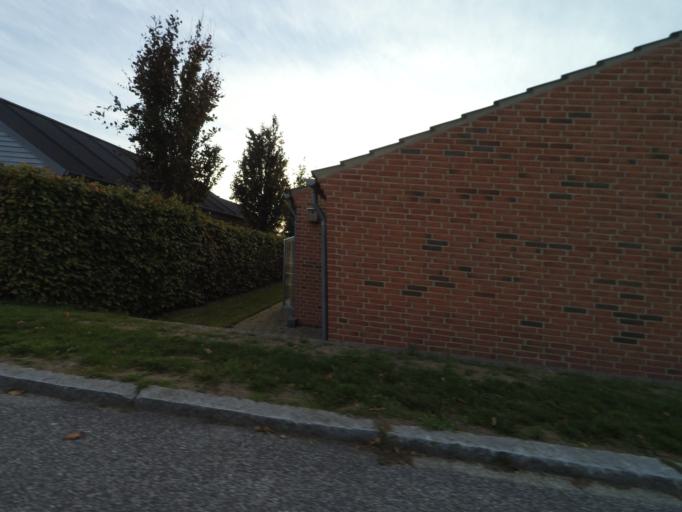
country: DK
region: Central Jutland
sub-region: Arhus Kommune
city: Stavtrup
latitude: 56.1613
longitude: 10.0990
